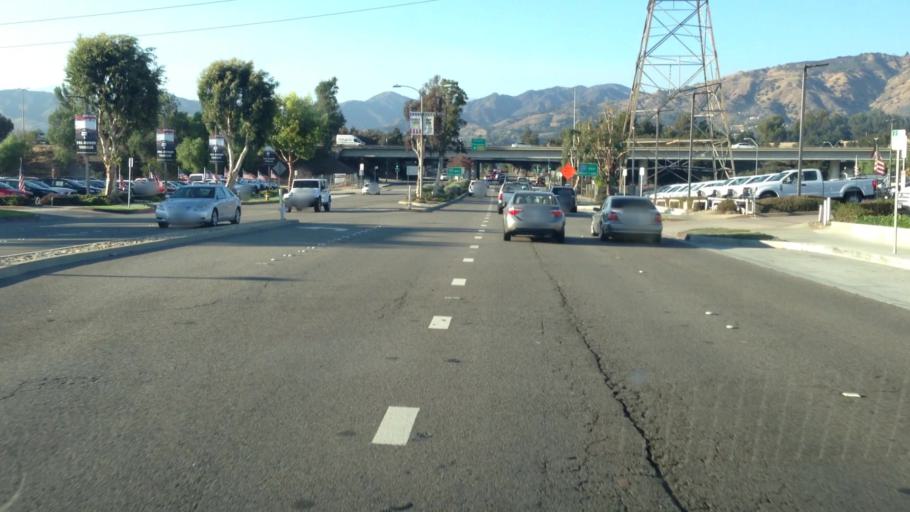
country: US
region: California
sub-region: Los Angeles County
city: Charter Oak
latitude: 34.1185
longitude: -117.8289
